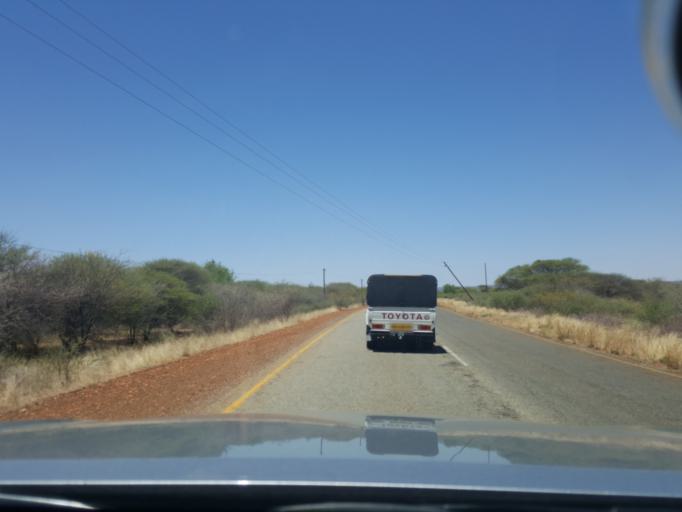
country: BW
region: South East
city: Otse
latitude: -25.1053
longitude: 25.9599
